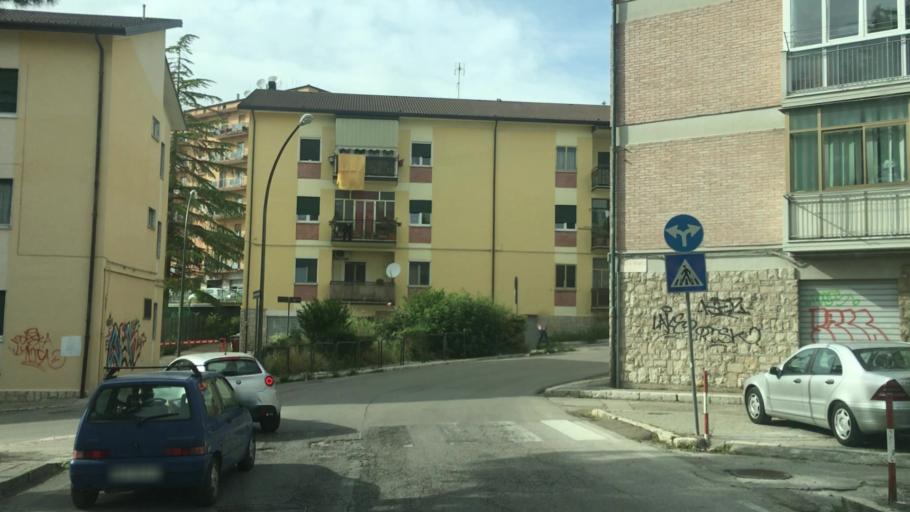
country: IT
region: Basilicate
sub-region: Provincia di Potenza
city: Potenza
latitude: 40.6450
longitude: 15.8003
